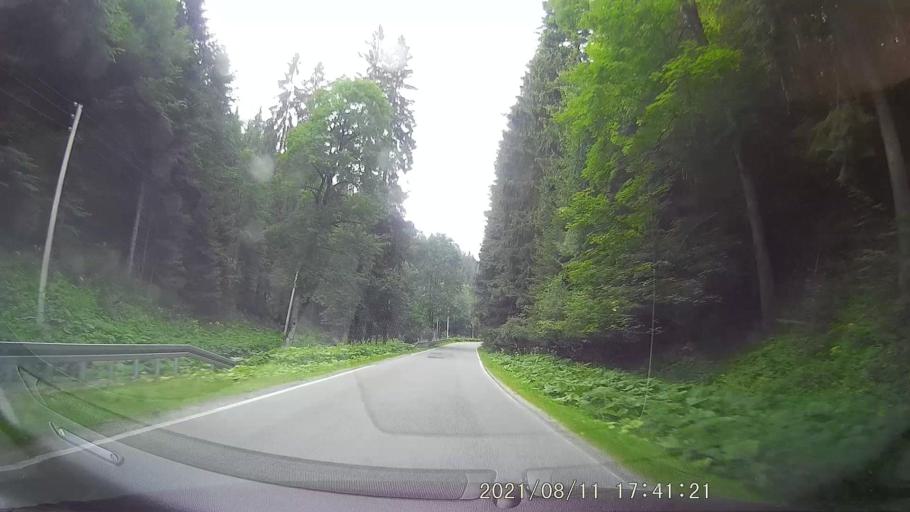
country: PL
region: Lower Silesian Voivodeship
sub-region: Powiat klodzki
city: Duszniki-Zdroj
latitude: 50.3662
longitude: 16.3916
